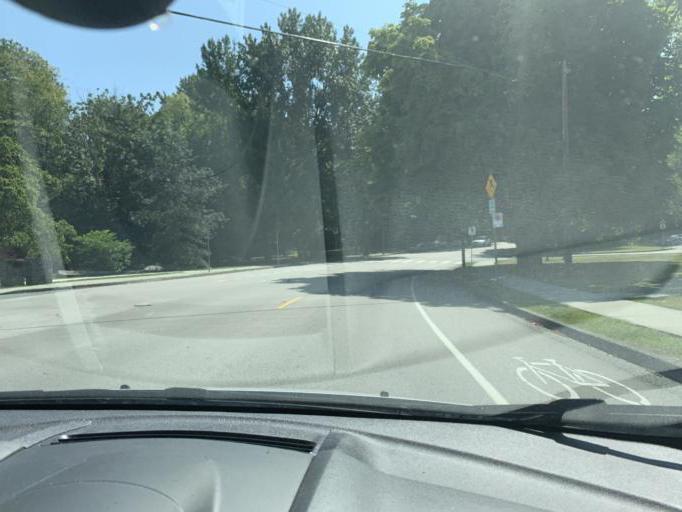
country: CA
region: British Columbia
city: West End
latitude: 49.2718
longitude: -123.2030
